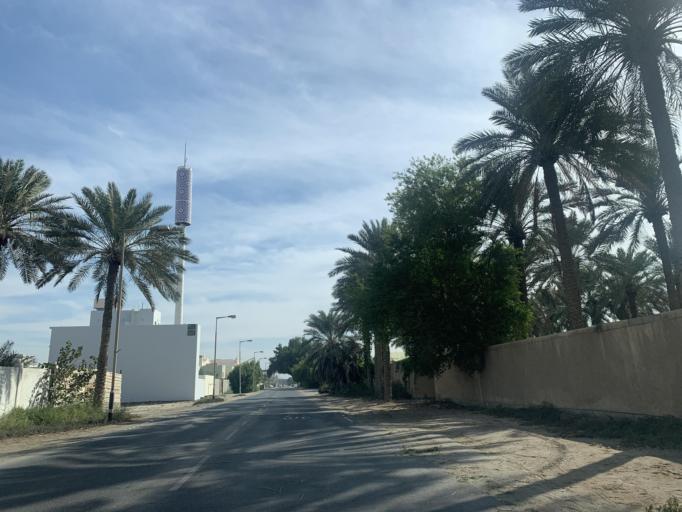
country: BH
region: Central Governorate
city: Madinat Hamad
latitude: 26.1238
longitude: 50.4723
